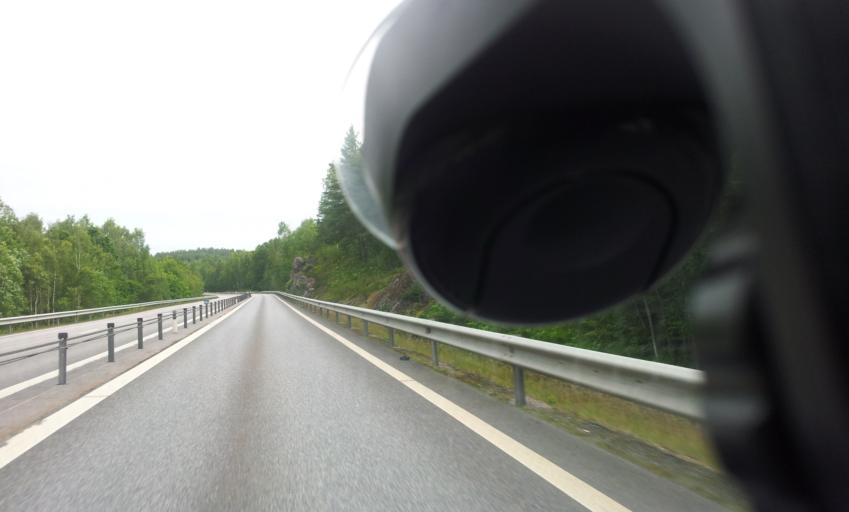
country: SE
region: OEstergoetland
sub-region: Valdemarsviks Kommun
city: Valdemarsvik
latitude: 58.1052
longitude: 16.5409
